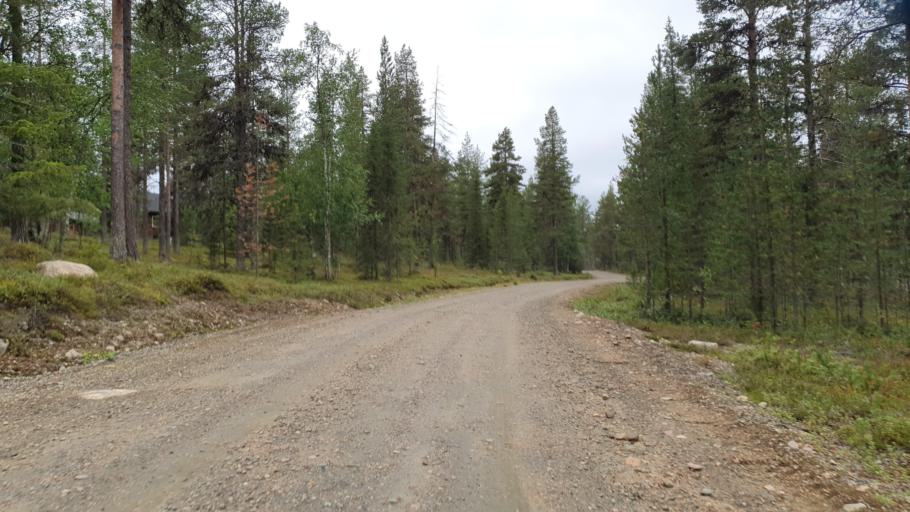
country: FI
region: Lapland
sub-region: Tunturi-Lappi
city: Kolari
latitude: 67.6002
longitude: 24.1953
